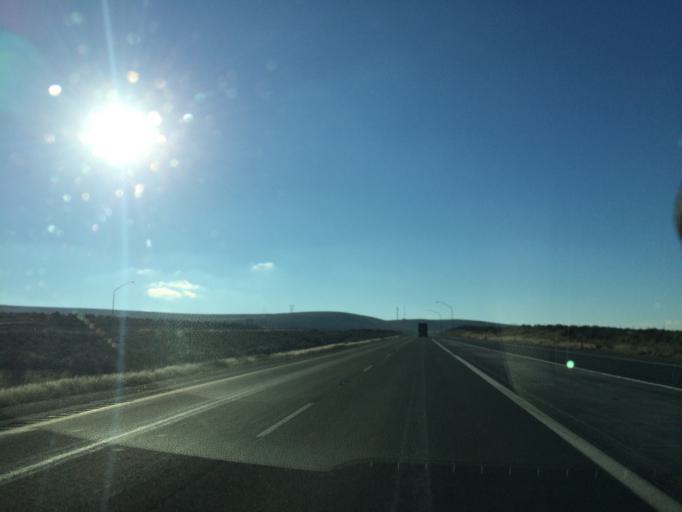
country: US
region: Washington
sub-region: Grant County
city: Quincy
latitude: 47.0181
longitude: -119.9473
